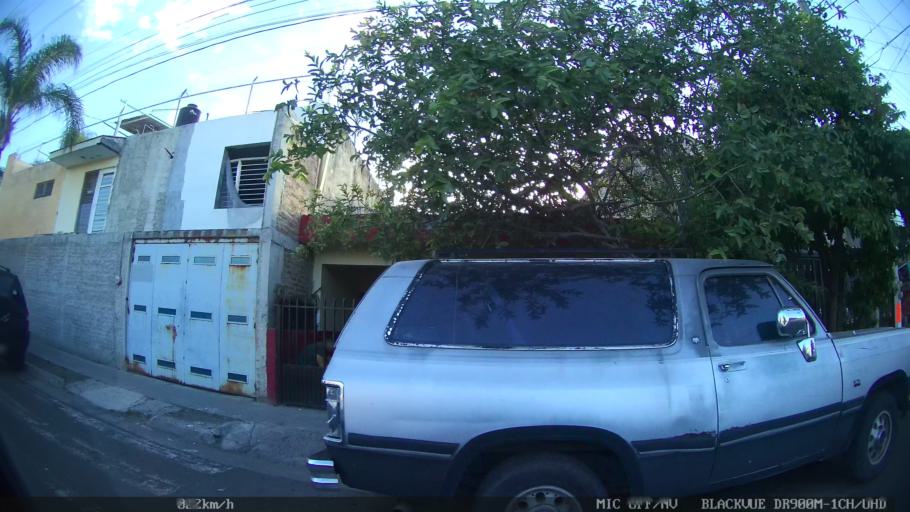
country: MX
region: Jalisco
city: Tlaquepaque
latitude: 20.7116
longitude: -103.2996
